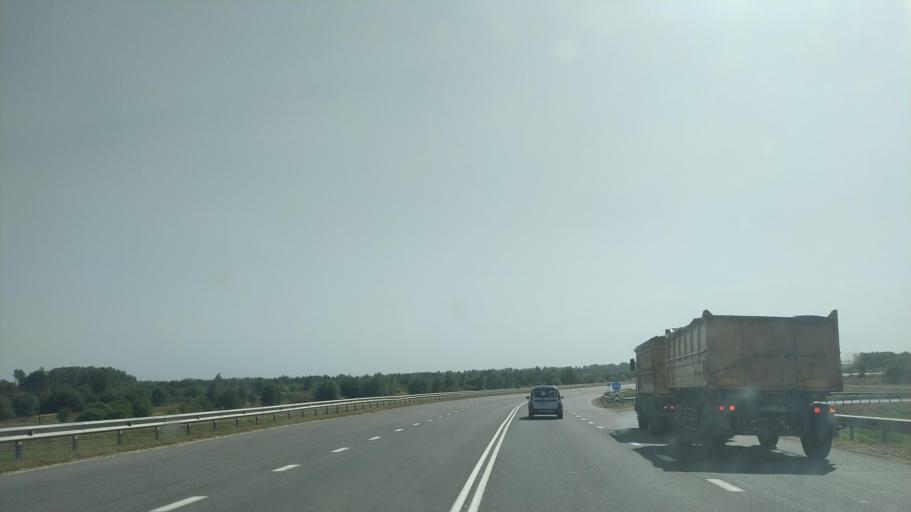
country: BY
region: Brest
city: Byaroza
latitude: 52.4887
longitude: 24.9693
